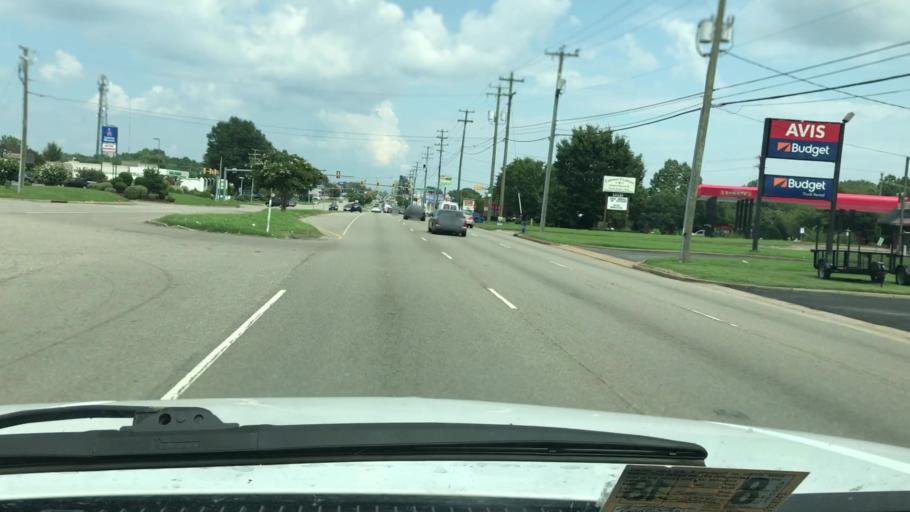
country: US
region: Virginia
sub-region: Chesterfield County
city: Bon Air
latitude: 37.4966
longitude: -77.5488
